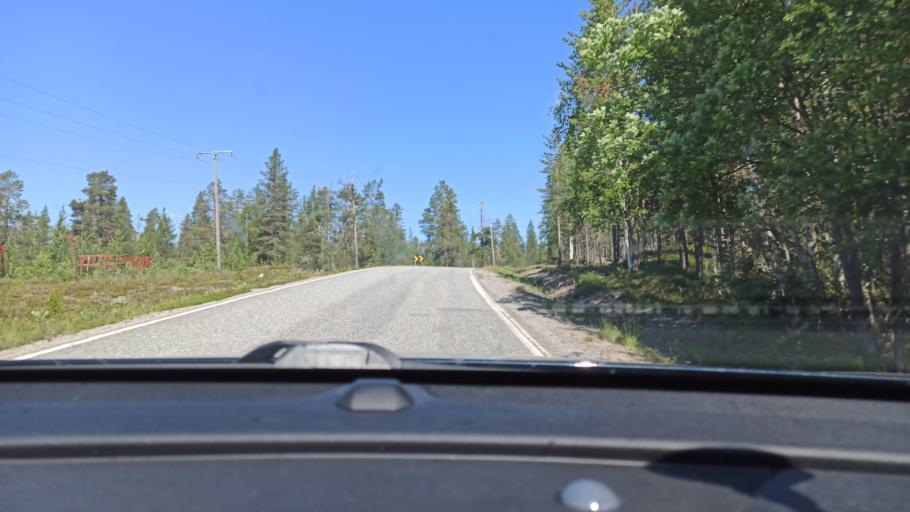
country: FI
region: Lapland
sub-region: Tunturi-Lappi
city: Kolari
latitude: 67.6366
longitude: 24.1570
